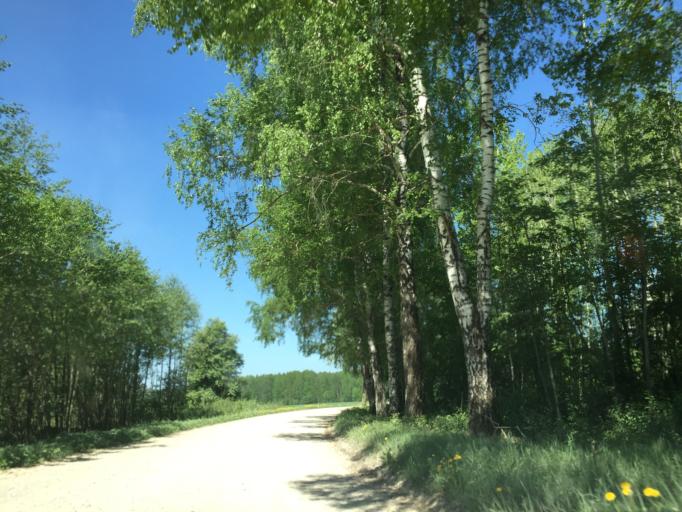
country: LV
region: Ikskile
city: Ikskile
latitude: 56.8718
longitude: 24.5008
